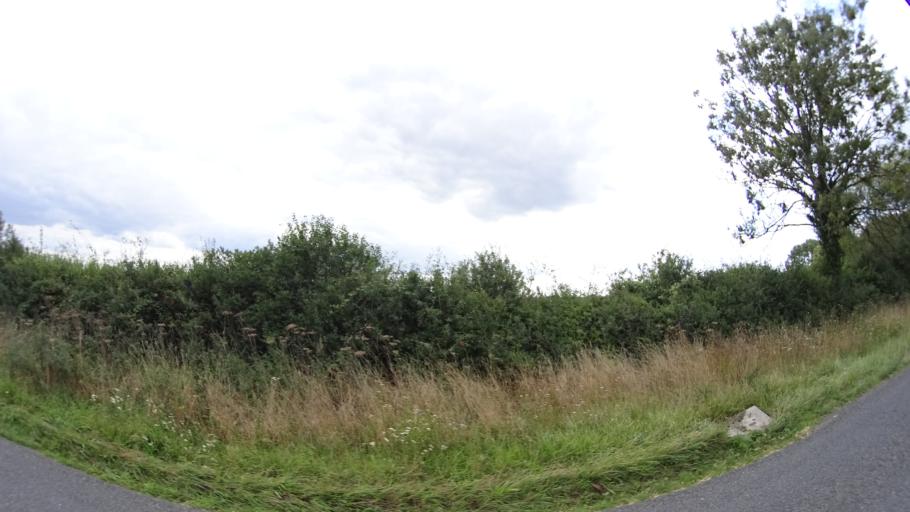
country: GB
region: England
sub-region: Wiltshire
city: Tidworth
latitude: 51.1780
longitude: -1.6450
